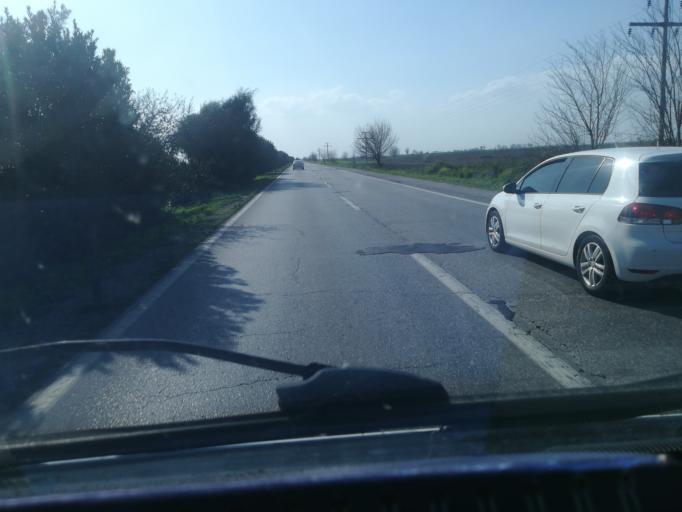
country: TR
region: Osmaniye
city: Toprakkale
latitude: 37.0736
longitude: 36.0488
